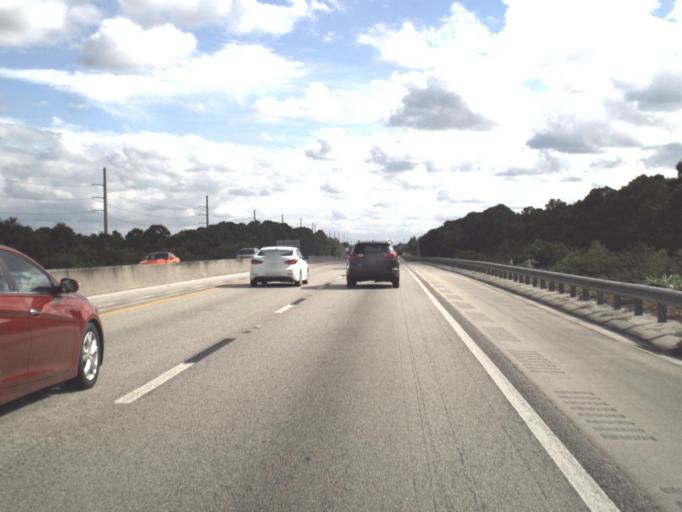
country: US
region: Florida
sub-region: Saint Lucie County
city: Port Saint Lucie
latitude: 27.2432
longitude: -80.3459
